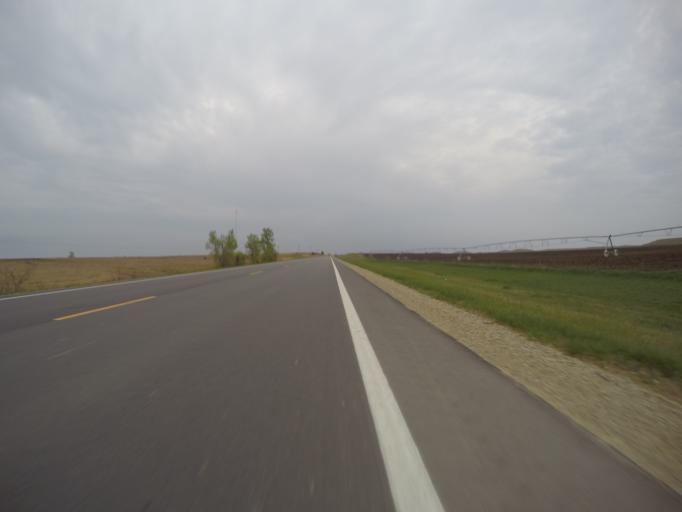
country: US
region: Kansas
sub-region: Pottawatomie County
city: Westmoreland
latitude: 39.3441
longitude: -96.5198
